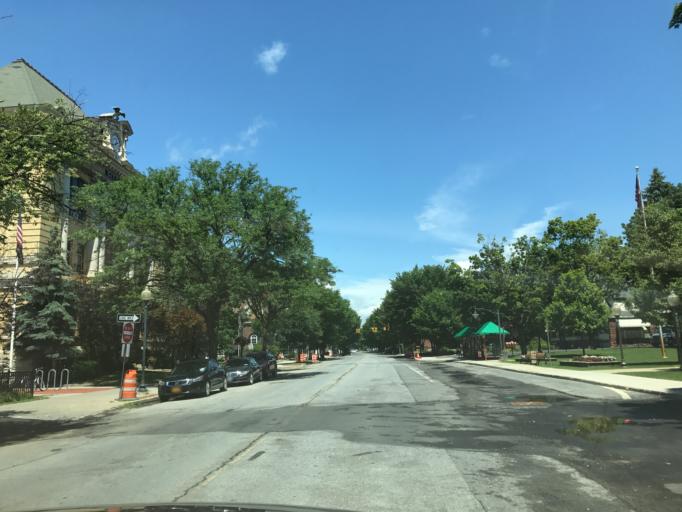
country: US
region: New York
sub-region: Warren County
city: Glens Falls
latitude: 43.3104
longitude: -73.6438
